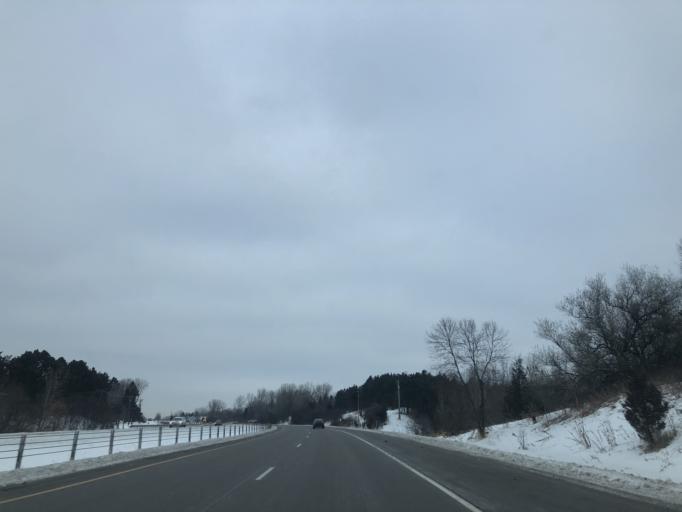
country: US
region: Minnesota
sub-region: Ramsey County
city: Shoreview
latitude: 45.0721
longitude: -93.1688
